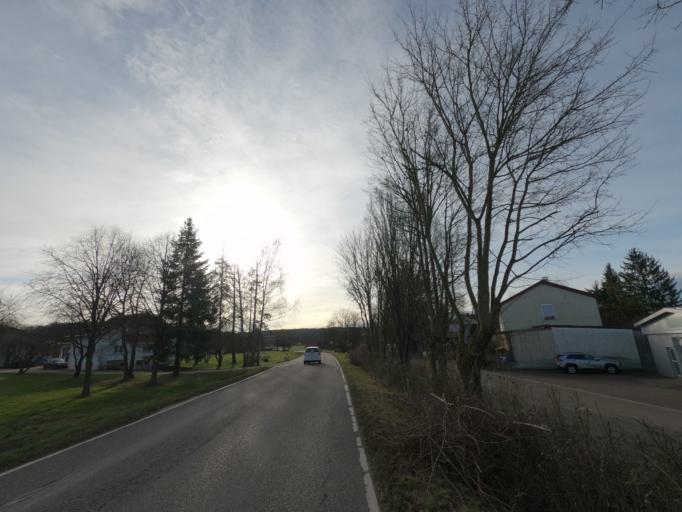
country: DE
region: Baden-Wuerttemberg
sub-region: Regierungsbezirk Stuttgart
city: Hattenhofen
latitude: 48.6797
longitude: 9.5876
